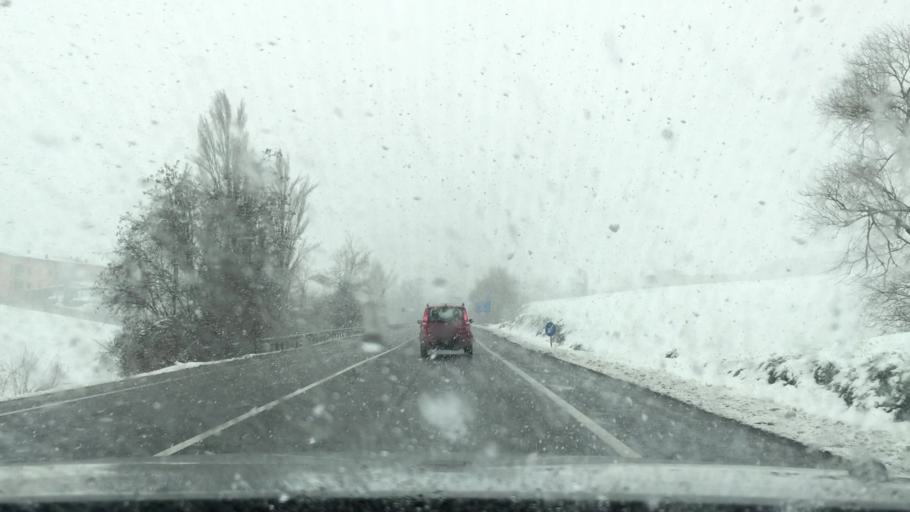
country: IT
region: Emilia-Romagna
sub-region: Provincia di Modena
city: Sant'Antonio
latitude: 44.4102
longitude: 10.8437
